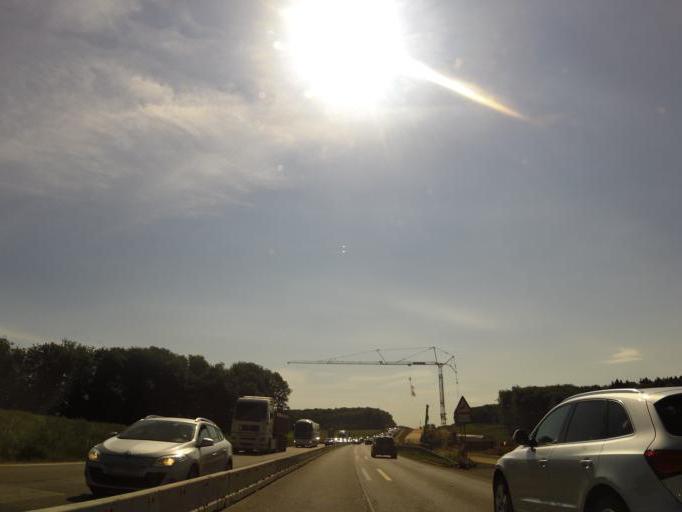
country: DE
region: Baden-Wuerttemberg
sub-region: Tuebingen Region
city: Nellingen
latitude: 48.5196
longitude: 9.8098
